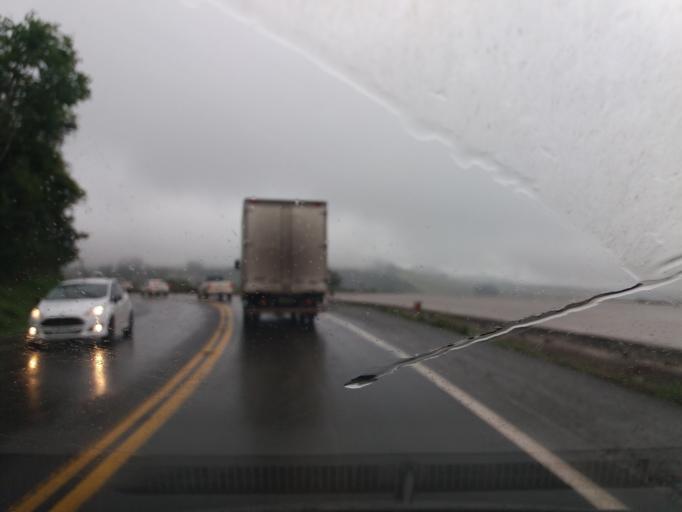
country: BR
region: Parana
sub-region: Realeza
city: Realeza
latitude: -25.4550
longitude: -53.5820
